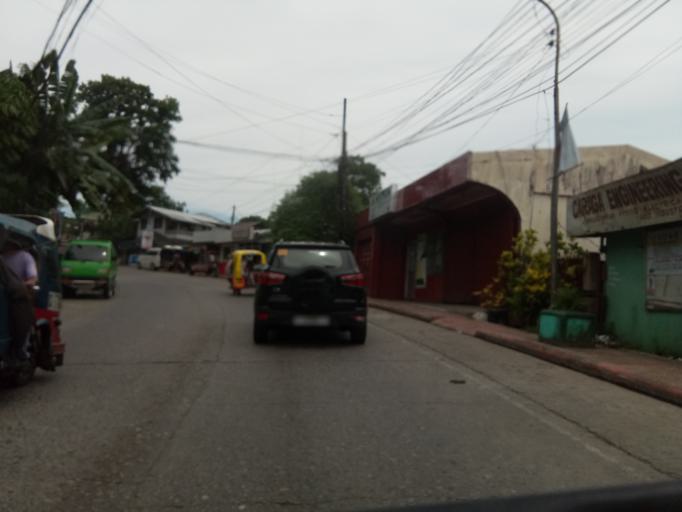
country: PH
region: Caraga
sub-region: Province of Surigao del Norte
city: Surigao
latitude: 9.7829
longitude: 125.4911
